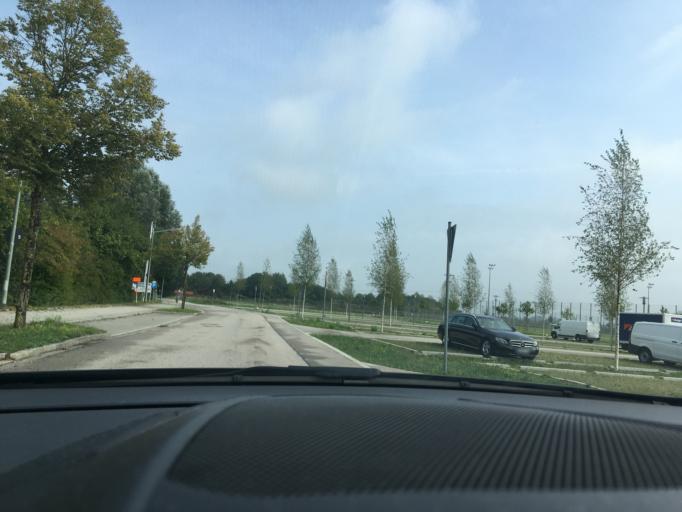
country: DE
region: Bavaria
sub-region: Upper Bavaria
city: Ismaning
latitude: 48.2411
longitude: 11.6852
